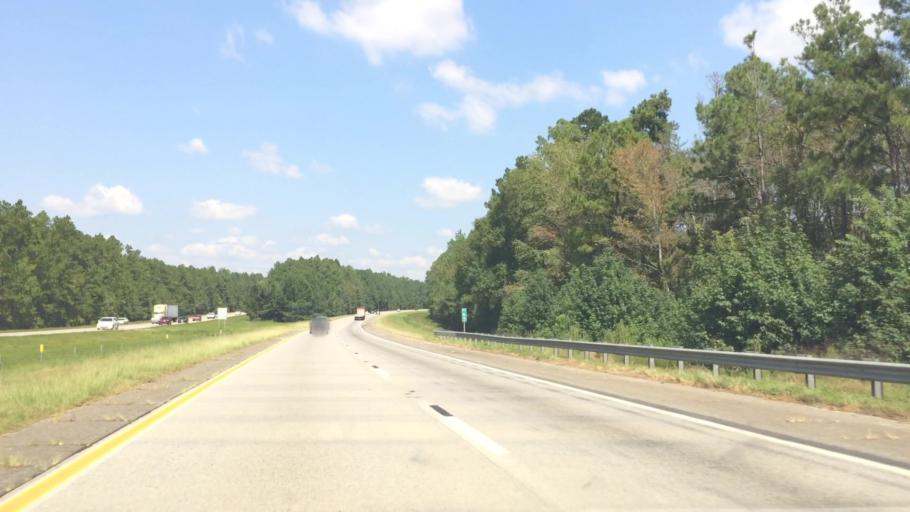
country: US
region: South Carolina
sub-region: Colleton County
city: Walterboro
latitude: 33.0381
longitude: -80.6688
